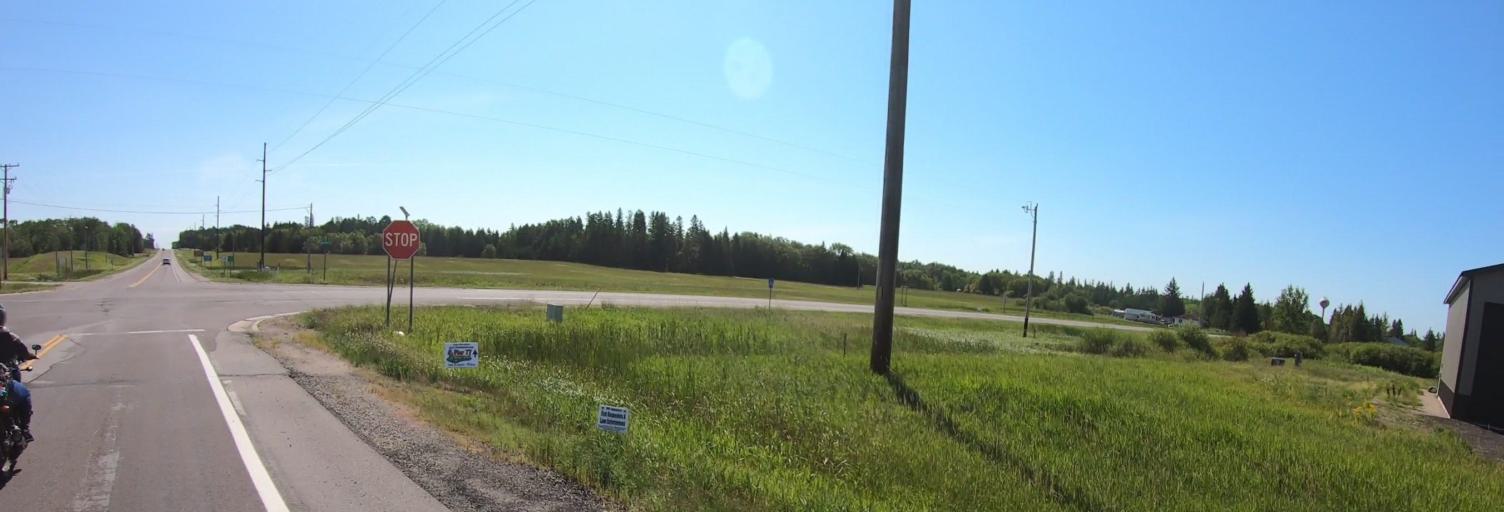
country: US
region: Minnesota
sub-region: Saint Louis County
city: Mountain Iron
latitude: 47.8609
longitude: -92.6862
